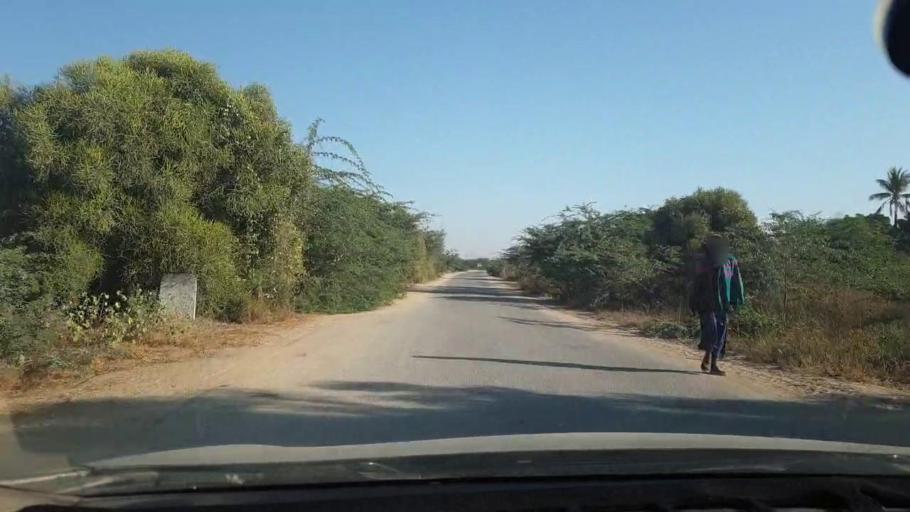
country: PK
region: Sindh
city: Malir Cantonment
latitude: 25.1739
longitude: 67.2025
